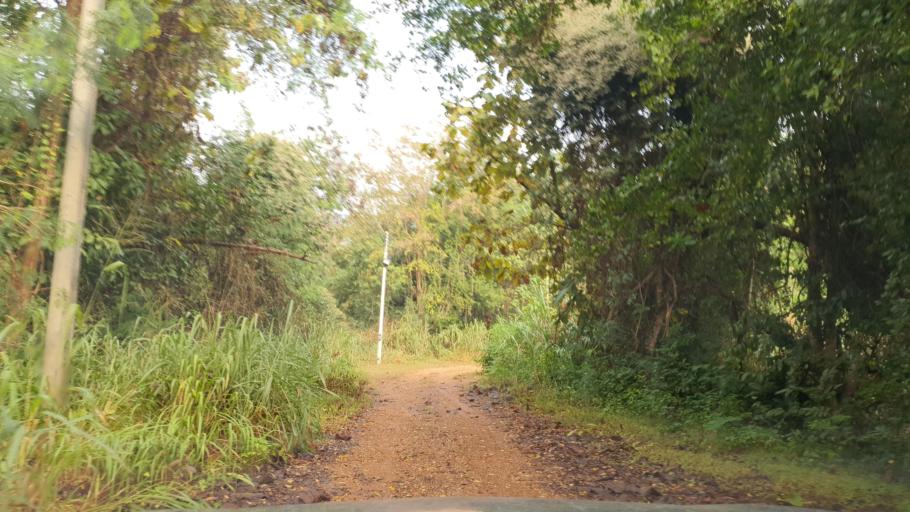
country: TH
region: Chiang Mai
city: Chiang Mai
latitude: 18.7684
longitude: 98.9285
